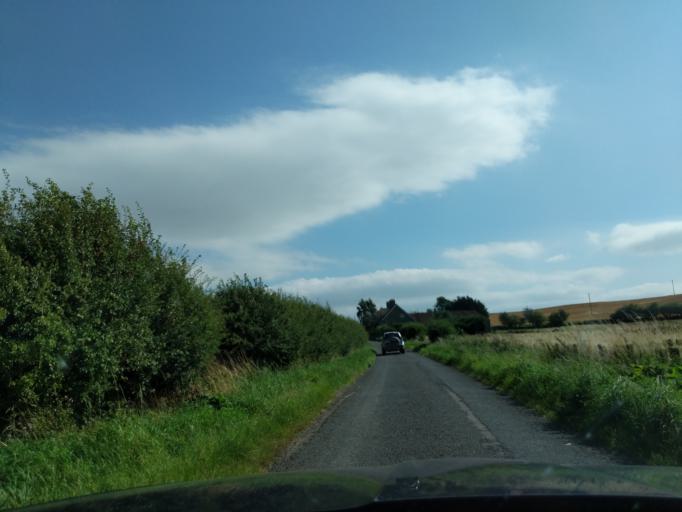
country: GB
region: England
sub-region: Northumberland
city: Ford
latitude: 55.6593
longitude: -2.1538
